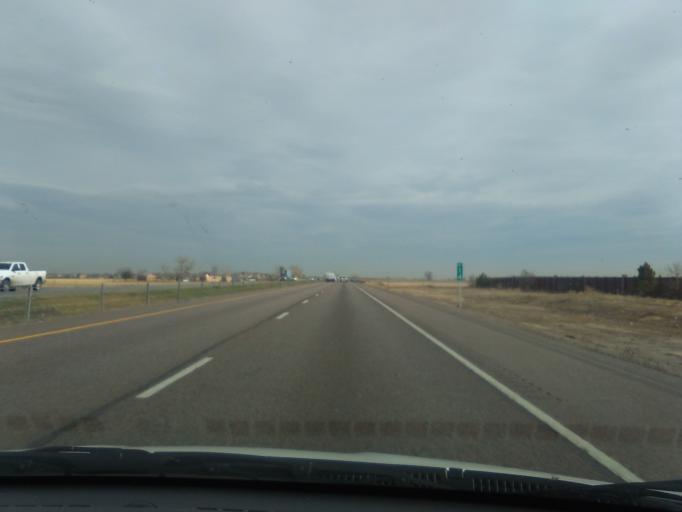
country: US
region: Colorado
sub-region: Adams County
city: Derby
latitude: 39.8878
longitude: -104.8628
